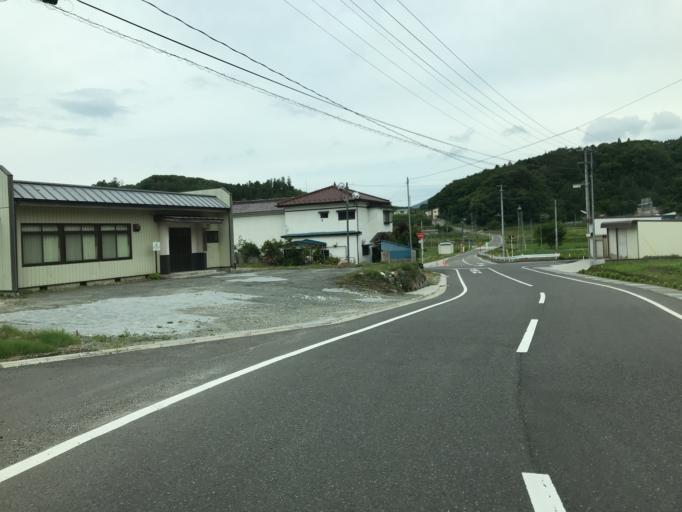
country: JP
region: Fukushima
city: Funehikimachi-funehiki
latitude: 37.4183
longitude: 140.6522
